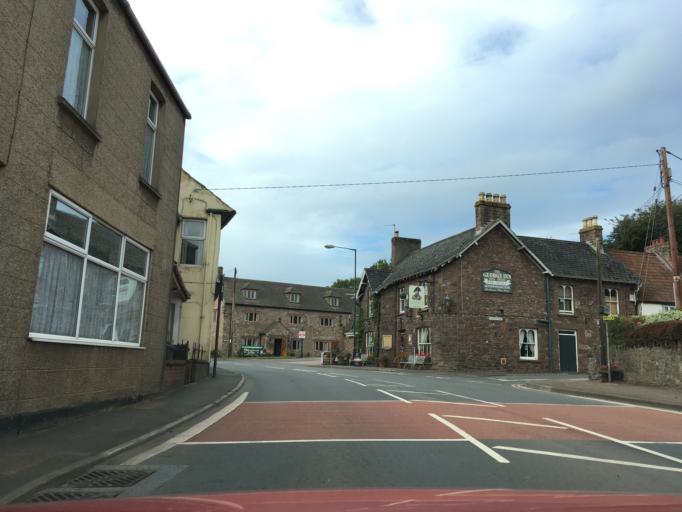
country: GB
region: England
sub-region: Gloucestershire
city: Lydney
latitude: 51.7147
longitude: -2.5536
